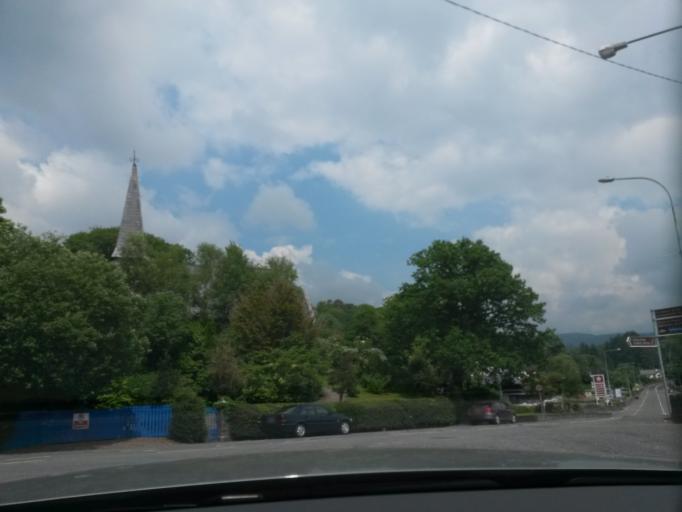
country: IE
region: Munster
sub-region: County Cork
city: Bantry
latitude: 51.7506
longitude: -9.5424
